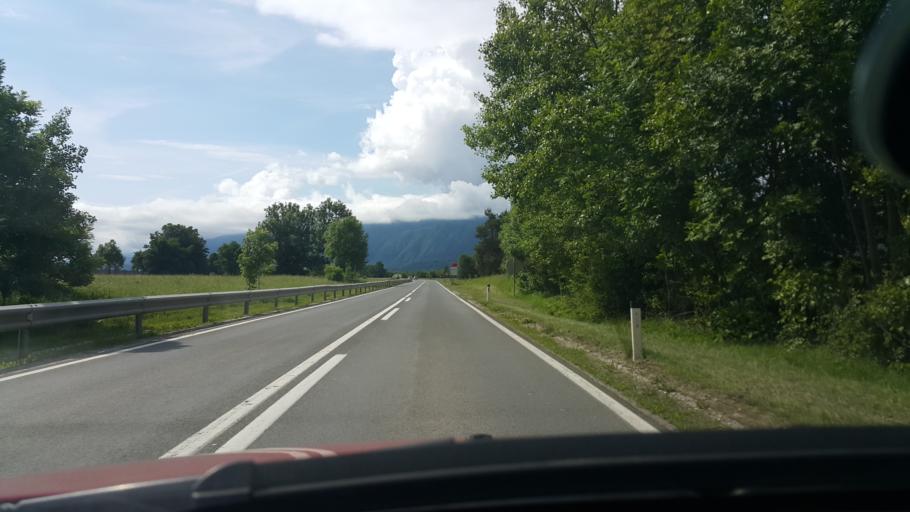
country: SI
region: Radovljica
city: Lesce
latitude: 46.3760
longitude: 14.1501
